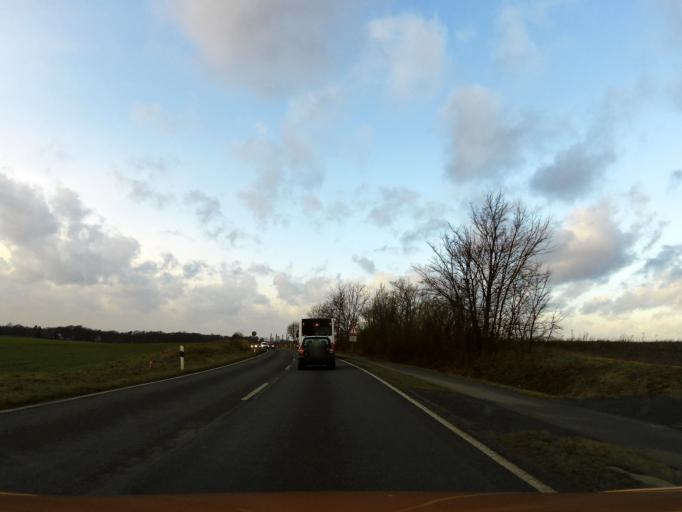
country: DE
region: Lower Saxony
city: Wolfsburg
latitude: 52.4100
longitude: 10.8245
